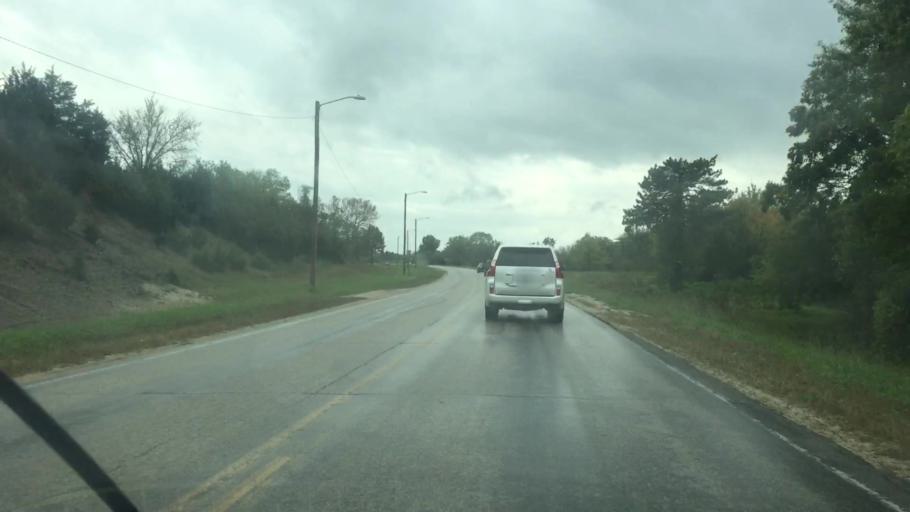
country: US
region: Kansas
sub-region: Allen County
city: Iola
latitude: 37.9075
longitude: -95.4098
